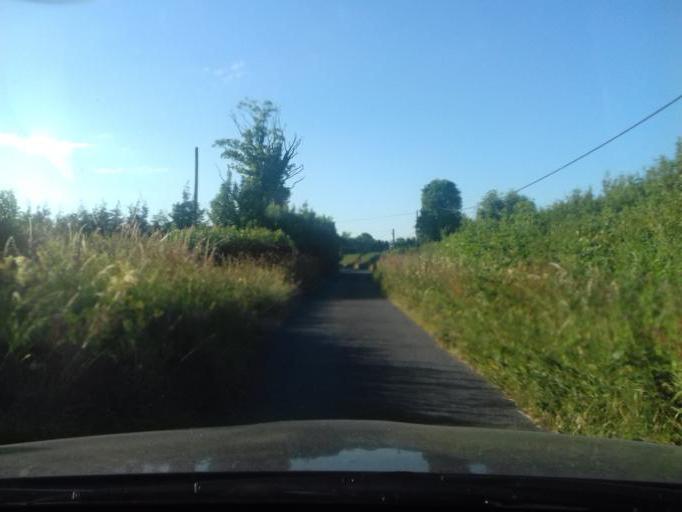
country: IE
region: Leinster
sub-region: An Mhi
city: Ashbourne
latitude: 53.4556
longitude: -6.3851
